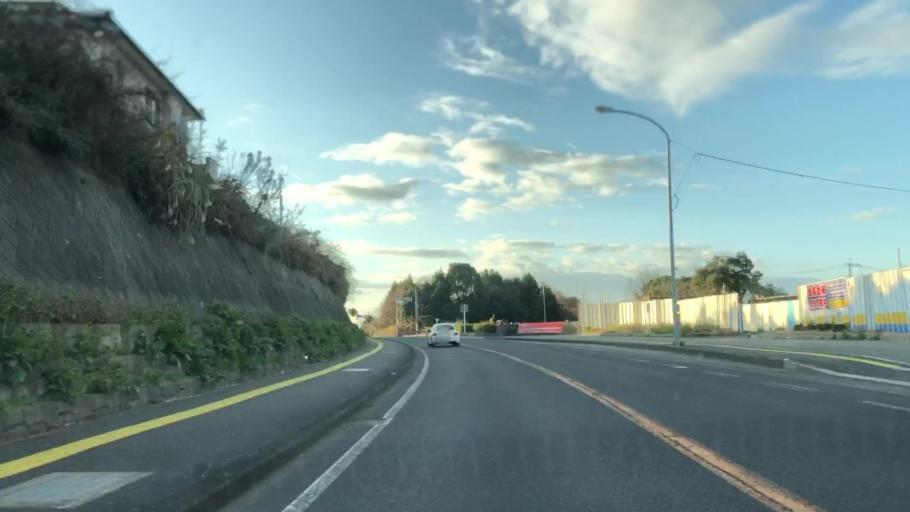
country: JP
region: Oita
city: Bungo-Takada-shi
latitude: 33.5358
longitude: 131.3116
